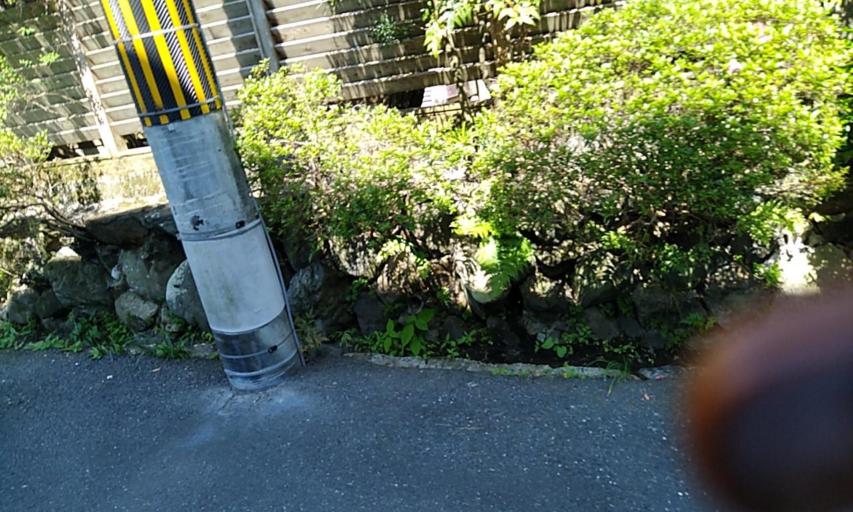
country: JP
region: Kyoto
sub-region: Kyoto-shi
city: Kamigyo-ku
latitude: 35.0208
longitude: 135.7956
